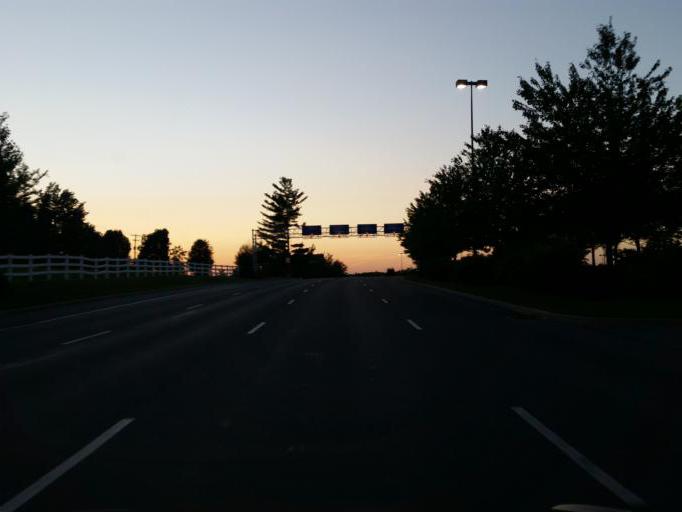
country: US
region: Pennsylvania
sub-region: Dauphin County
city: Hershey
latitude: 40.2835
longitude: -76.6723
